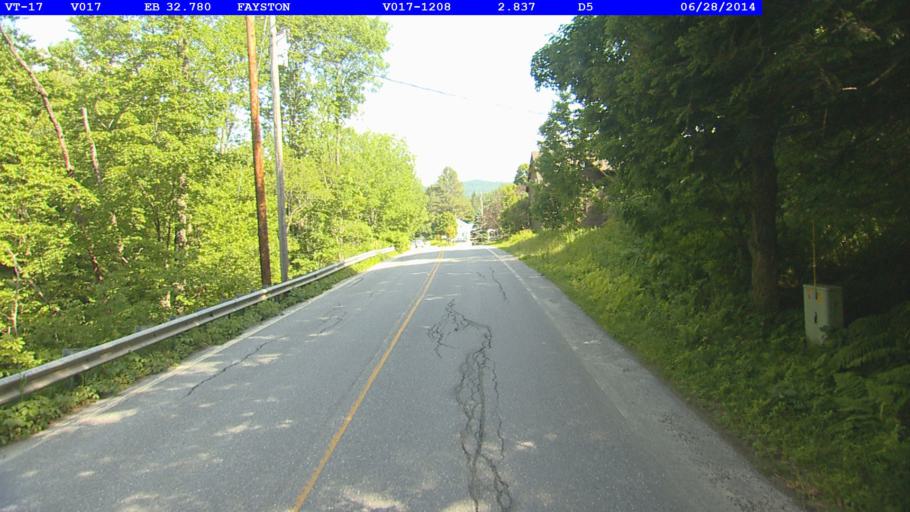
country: US
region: Vermont
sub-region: Washington County
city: Waterbury
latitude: 44.1972
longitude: -72.8929
